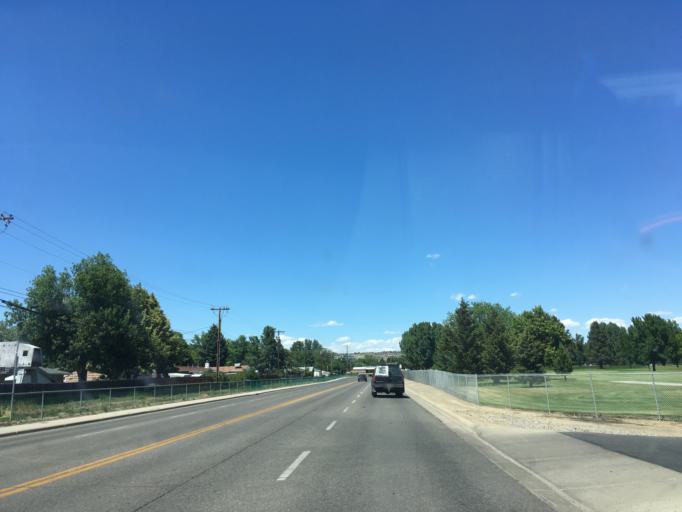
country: US
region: Montana
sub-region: Yellowstone County
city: Billings
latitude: 45.7662
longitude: -108.5650
